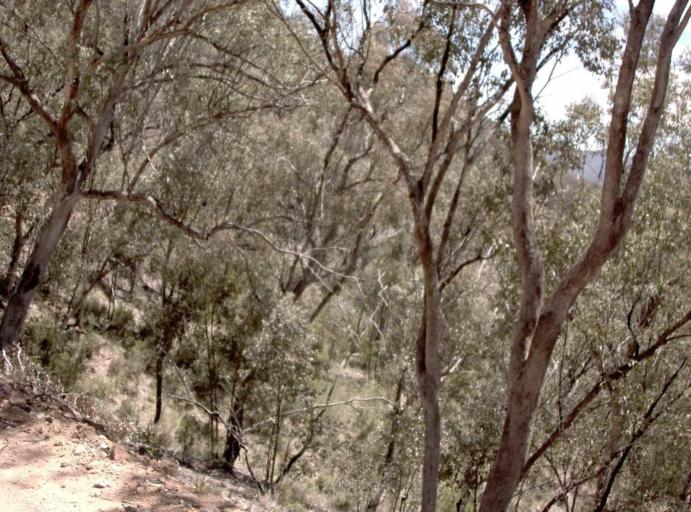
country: AU
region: New South Wales
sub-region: Snowy River
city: Jindabyne
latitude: -36.9785
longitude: 148.3016
